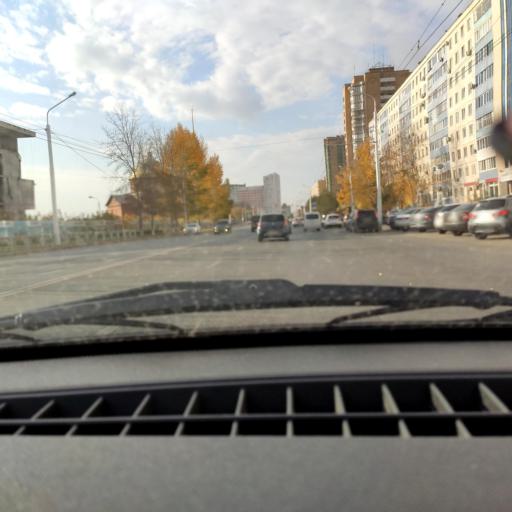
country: RU
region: Bashkortostan
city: Ufa
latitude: 54.7665
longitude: 56.0277
